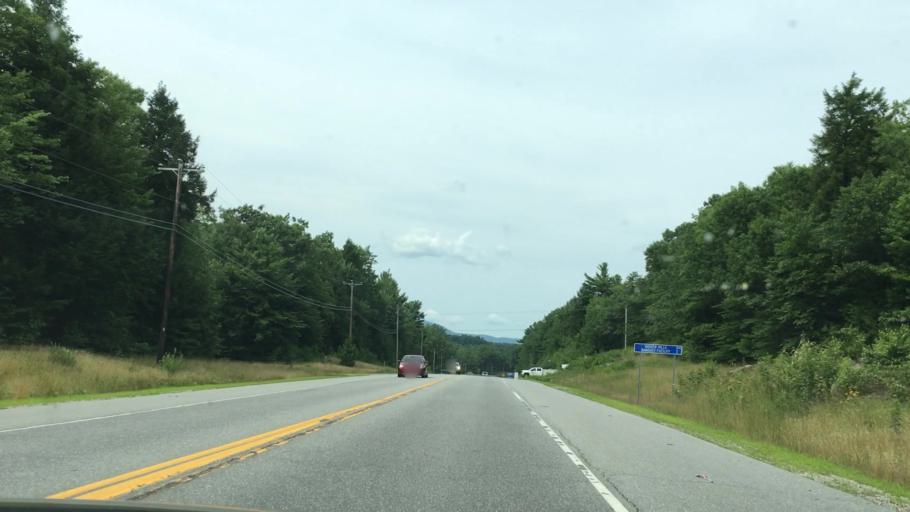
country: US
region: New Hampshire
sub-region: Cheshire County
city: Rindge
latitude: 42.7456
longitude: -72.0384
